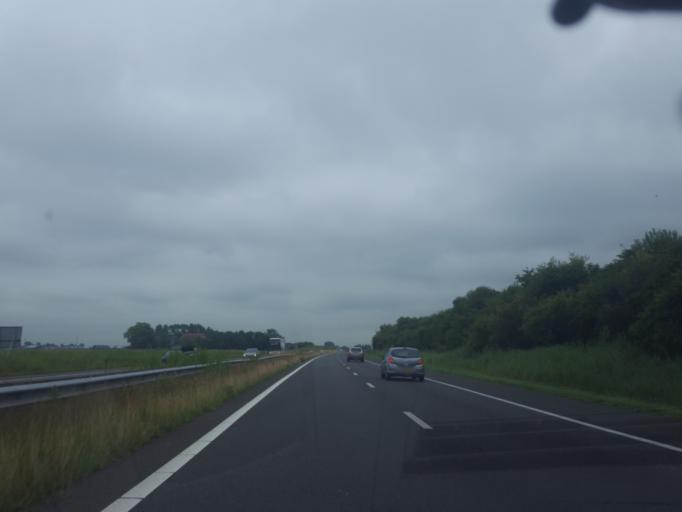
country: NL
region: Friesland
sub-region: Gemeente Boarnsterhim
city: Reduzum
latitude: 53.1115
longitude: 5.8133
